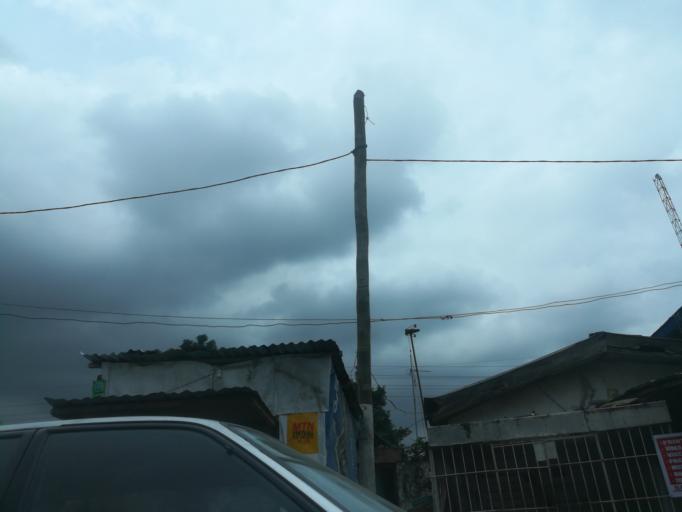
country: NG
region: Lagos
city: Ikeja
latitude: 6.5950
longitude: 3.3427
